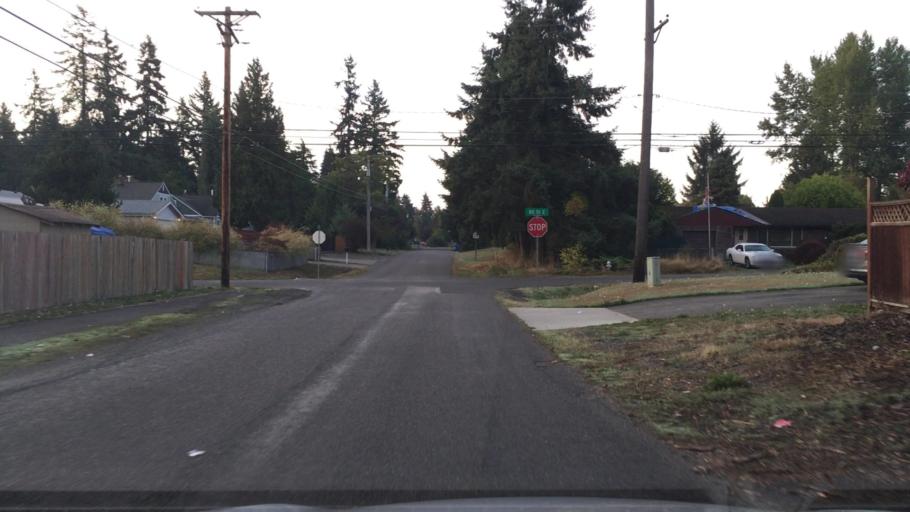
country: US
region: Washington
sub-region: Pierce County
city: Midland
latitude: 47.1848
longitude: -122.4026
